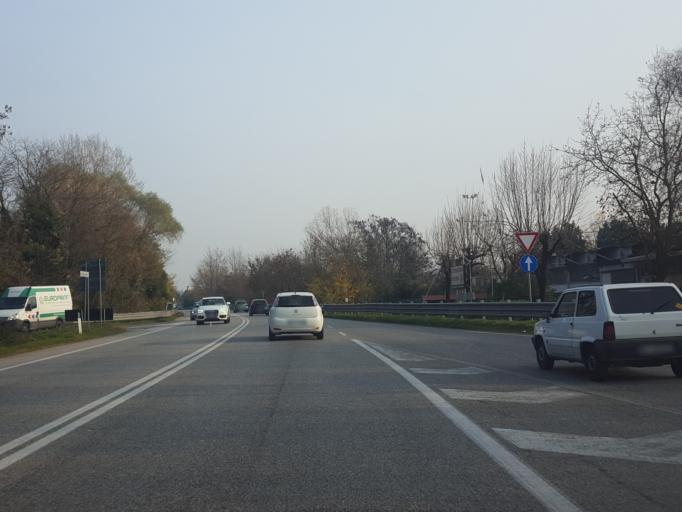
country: IT
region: Veneto
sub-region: Provincia di Treviso
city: Silea
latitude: 45.6514
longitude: 12.2974
